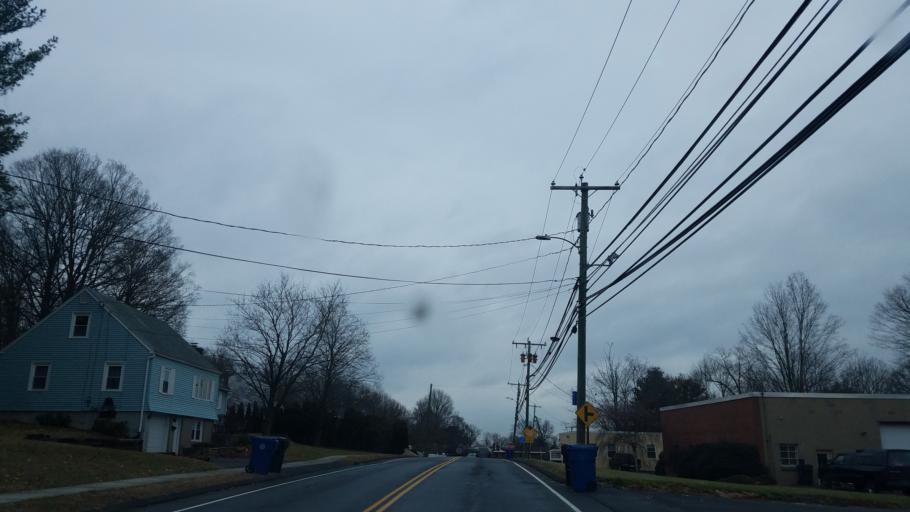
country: US
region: Connecticut
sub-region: Hartford County
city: Kensington
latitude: 41.6281
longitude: -72.7706
